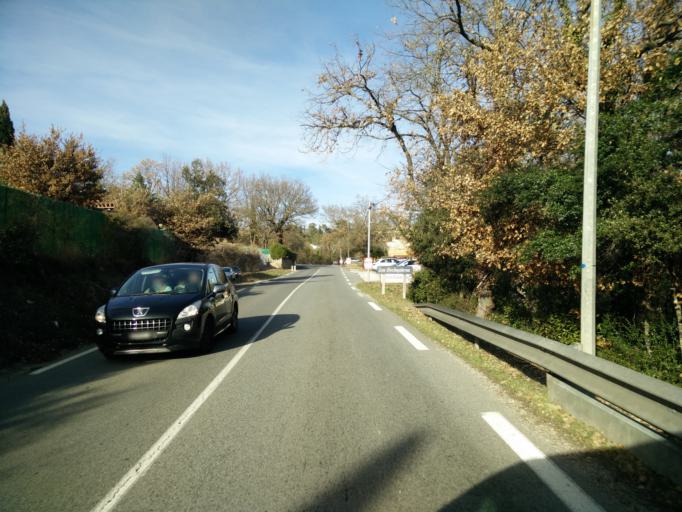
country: FR
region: Provence-Alpes-Cote d'Azur
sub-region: Departement du Var
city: Montauroux
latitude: 43.5928
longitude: 6.7896
